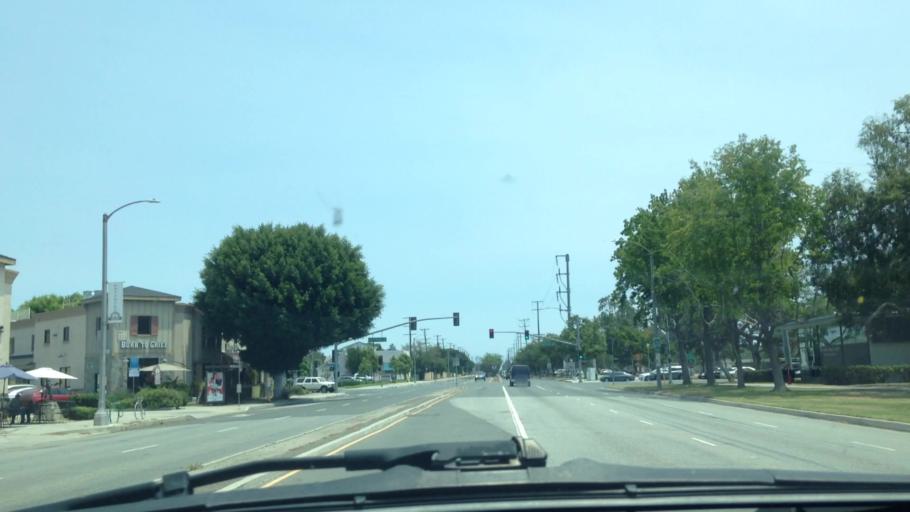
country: US
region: California
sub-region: Los Angeles County
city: Lakewood
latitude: 33.8323
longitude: -118.1265
